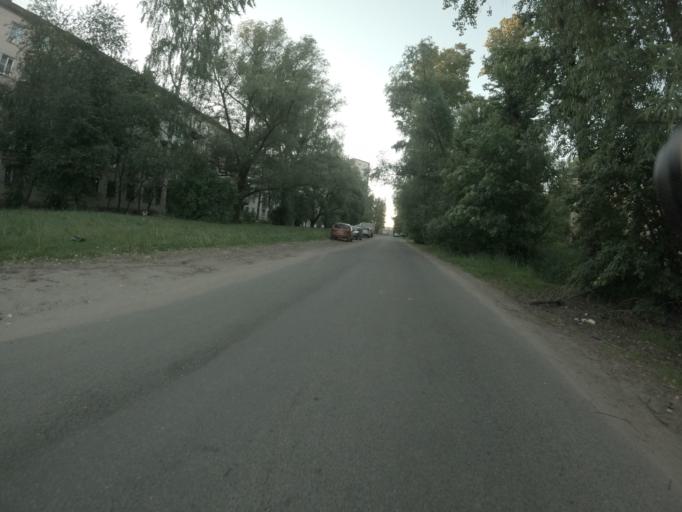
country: RU
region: St.-Petersburg
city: Krasnogvargeisky
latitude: 59.9770
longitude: 30.5143
